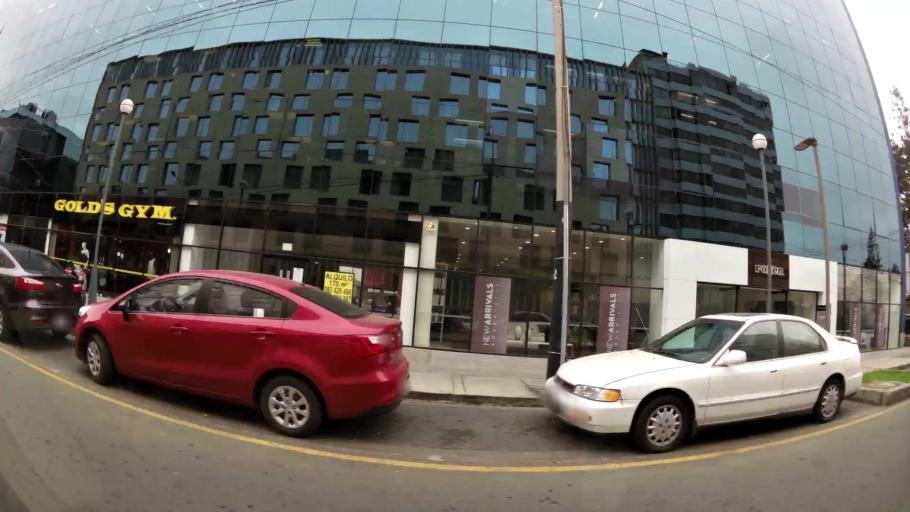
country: PE
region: Lima
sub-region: Lima
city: San Isidro
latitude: -12.0948
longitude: -77.0378
